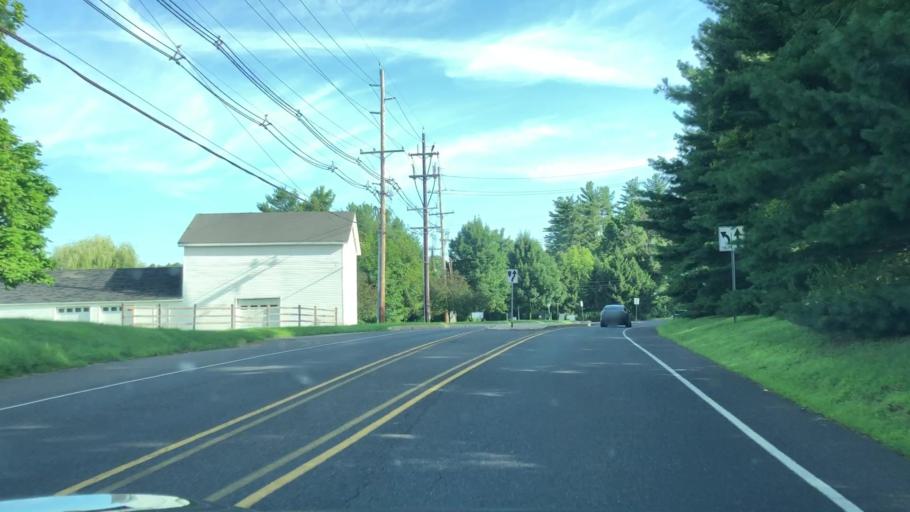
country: US
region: New Jersey
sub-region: Mercer County
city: Pennington
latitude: 40.3458
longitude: -74.7635
